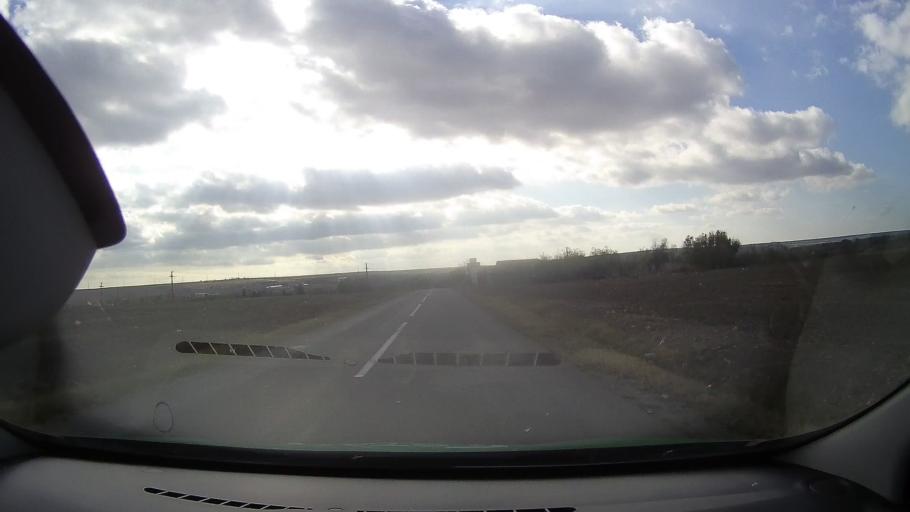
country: RO
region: Constanta
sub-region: Comuna Sacele
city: Sacele
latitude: 44.4916
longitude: 28.6538
